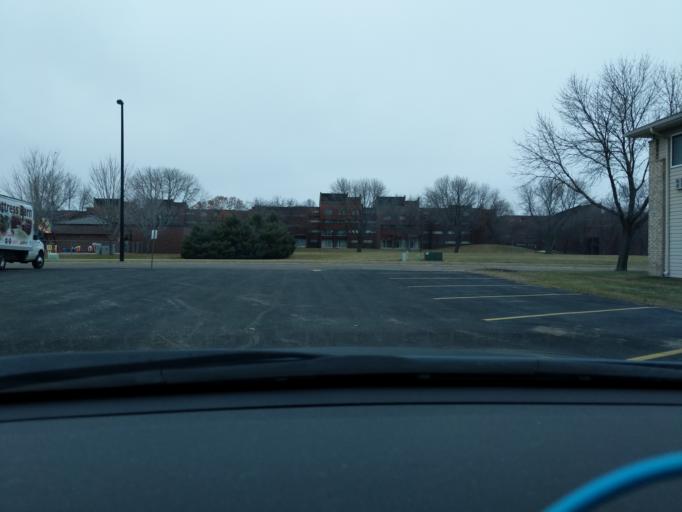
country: US
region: Minnesota
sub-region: Lyon County
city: Marshall
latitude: 44.4512
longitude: -95.7601
